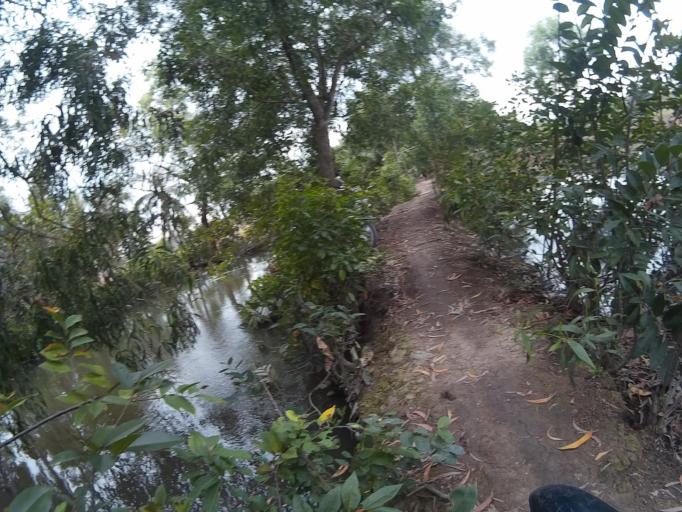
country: VN
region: Ho Chi Minh City
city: Quan Hai
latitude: 10.8116
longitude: 106.7403
